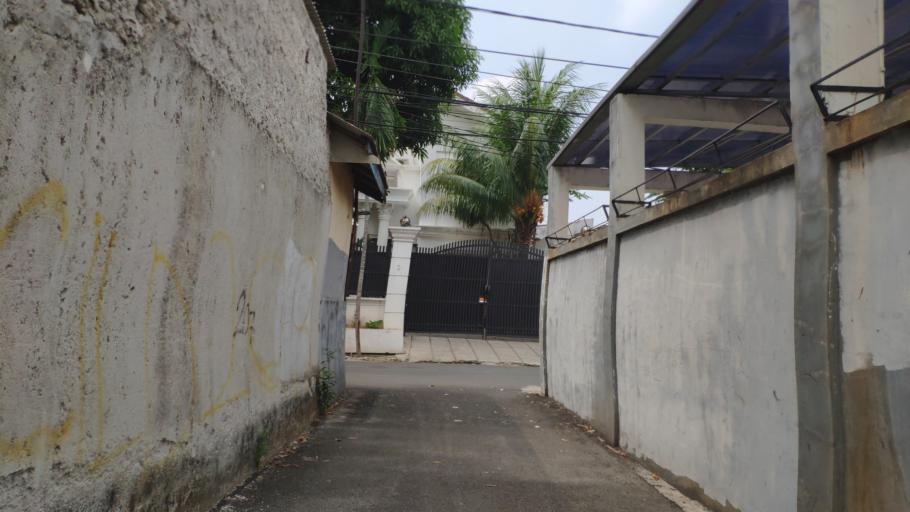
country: ID
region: Banten
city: South Tangerang
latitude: -6.2687
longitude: 106.7731
